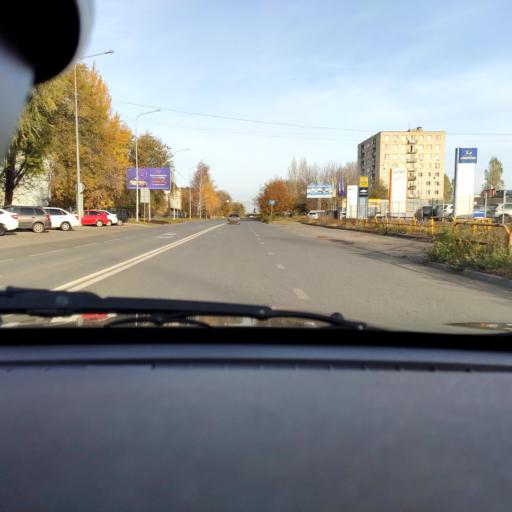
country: RU
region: Samara
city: Tol'yatti
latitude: 53.5378
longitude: 49.4098
